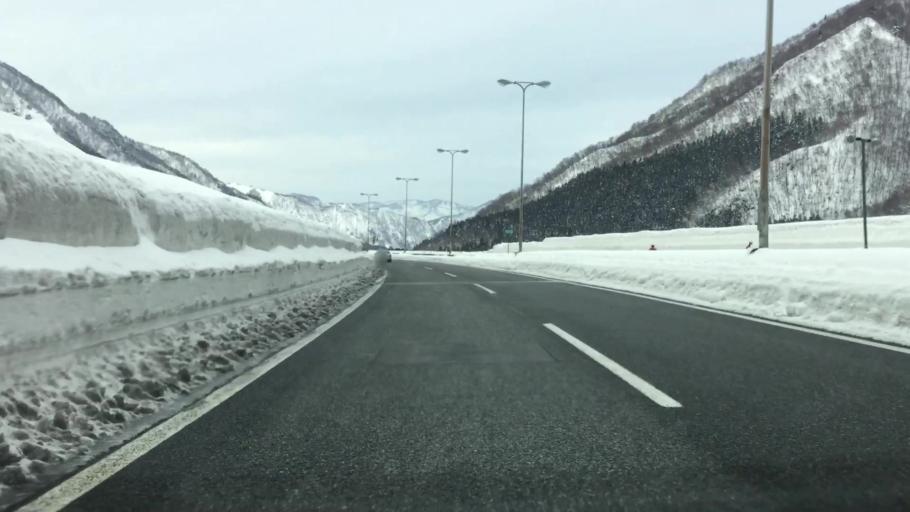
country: JP
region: Niigata
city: Shiozawa
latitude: 36.8738
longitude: 138.8638
